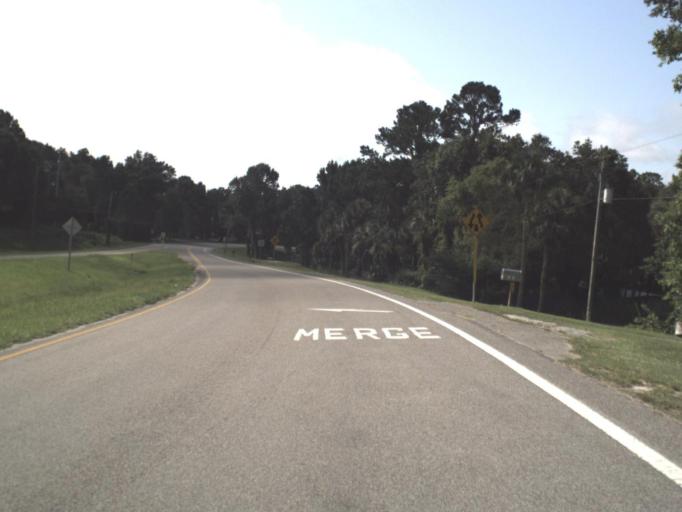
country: US
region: Florida
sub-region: Hernando County
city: North Brooksville
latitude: 28.5759
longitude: -82.3999
